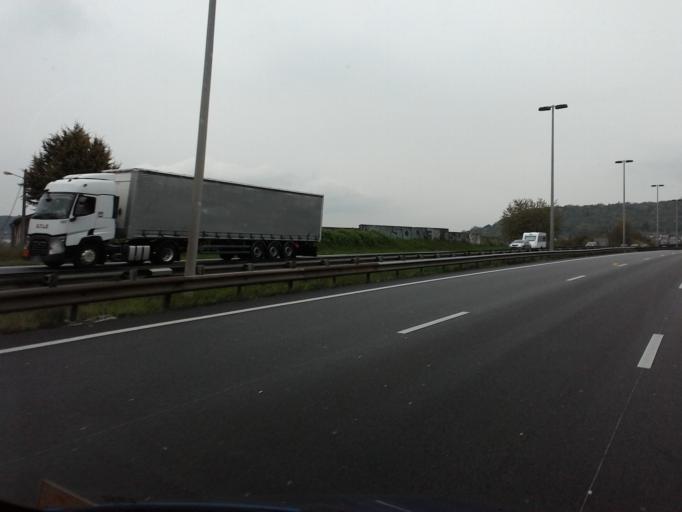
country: FR
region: Lorraine
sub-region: Departement de Meurthe-et-Moselle
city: Champigneulles
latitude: 48.7348
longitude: 6.1570
